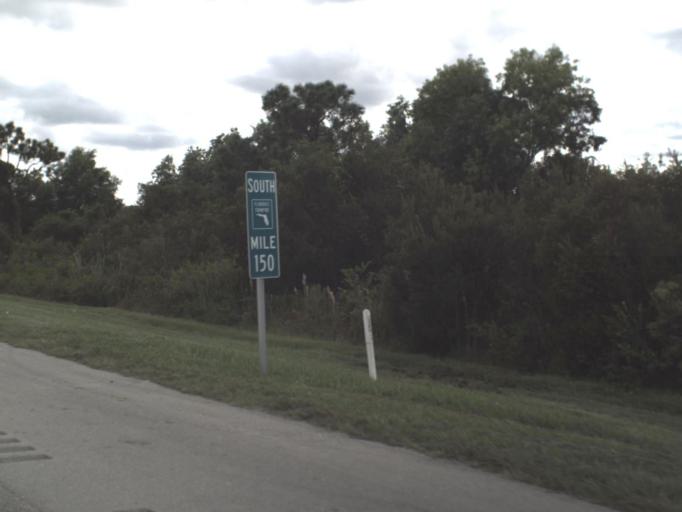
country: US
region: Florida
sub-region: Saint Lucie County
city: White City
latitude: 27.3696
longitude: -80.3816
